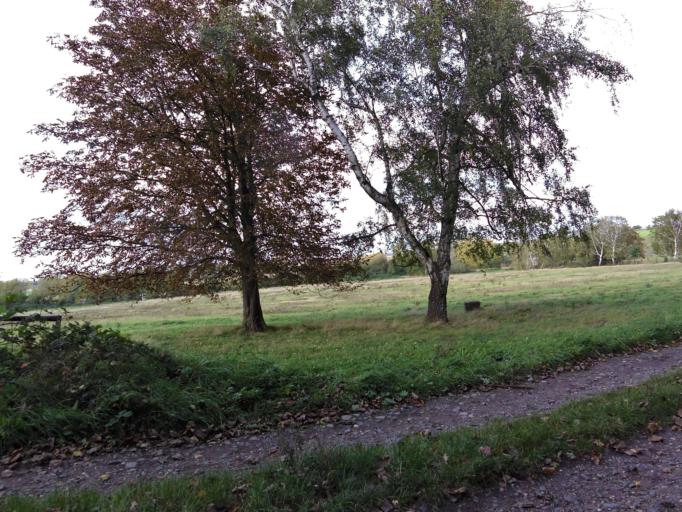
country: DE
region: Saxony
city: Grossposna
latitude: 51.2909
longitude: 12.4912
